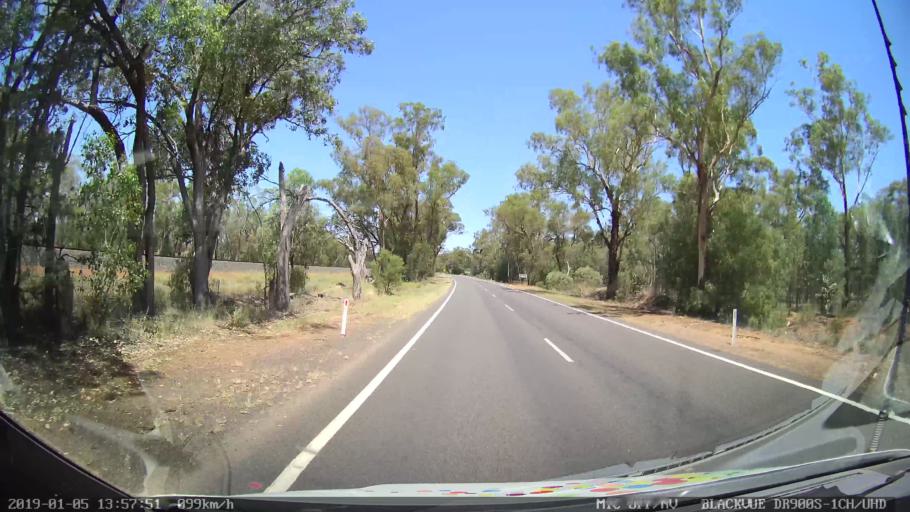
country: AU
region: New South Wales
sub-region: Gunnedah
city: Gunnedah
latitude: -31.1324
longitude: 150.2775
